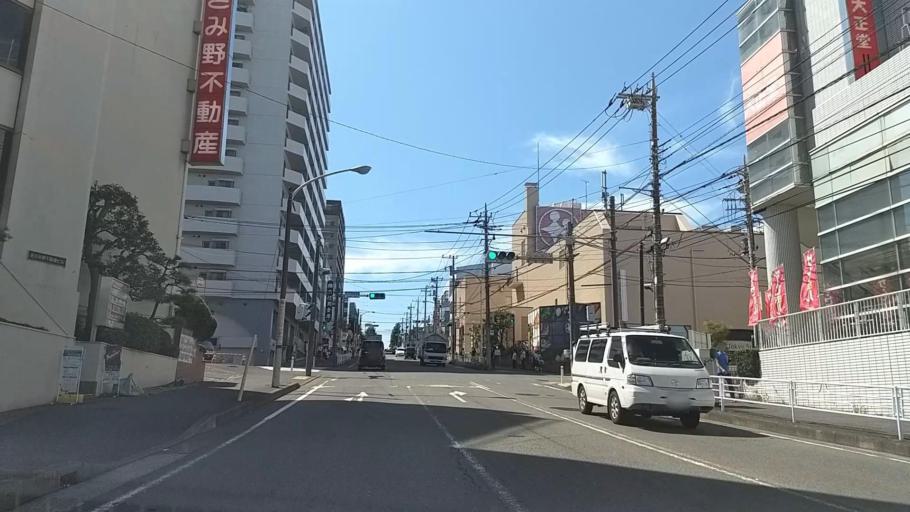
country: JP
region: Tokyo
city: Chofugaoka
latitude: 35.5693
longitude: 139.5544
